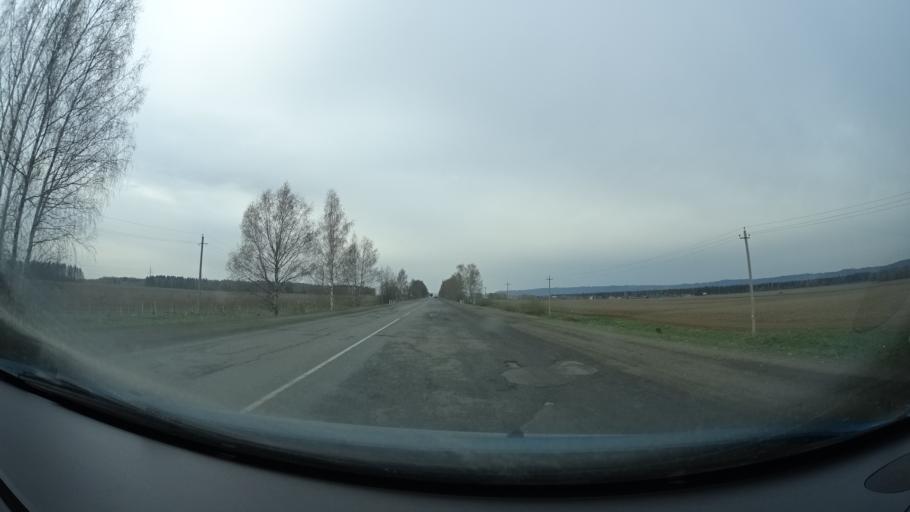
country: RU
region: Perm
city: Ust'-Kachka
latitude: 58.0572
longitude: 55.6061
